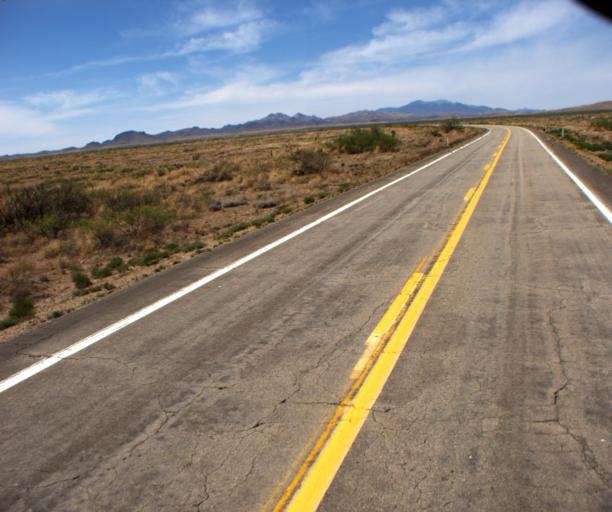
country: US
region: Arizona
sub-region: Cochise County
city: Willcox
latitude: 32.3669
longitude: -109.6234
